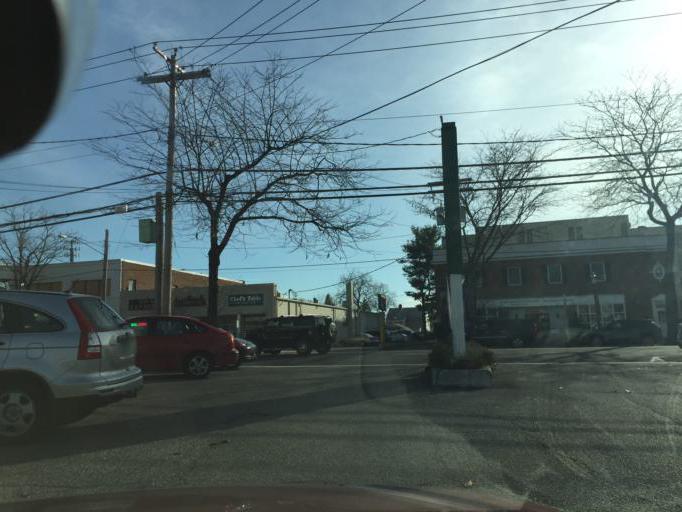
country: US
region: Connecticut
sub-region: Fairfield County
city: Fairfield
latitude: 41.1413
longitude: -73.2593
